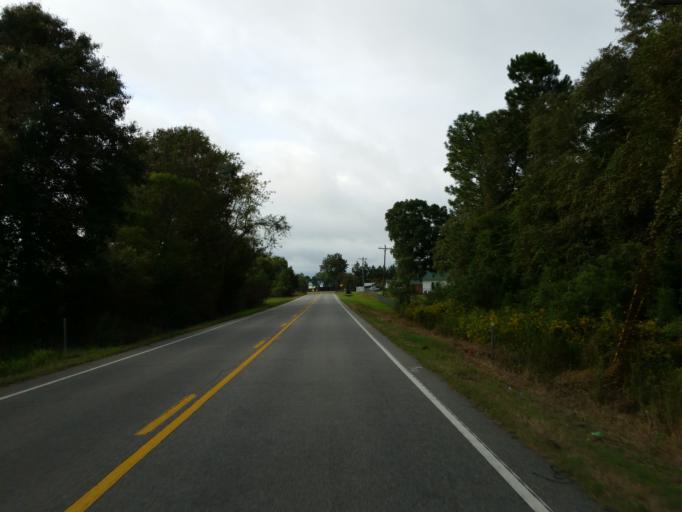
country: US
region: Georgia
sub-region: Turner County
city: Ashburn
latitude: 31.5854
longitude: -83.5747
